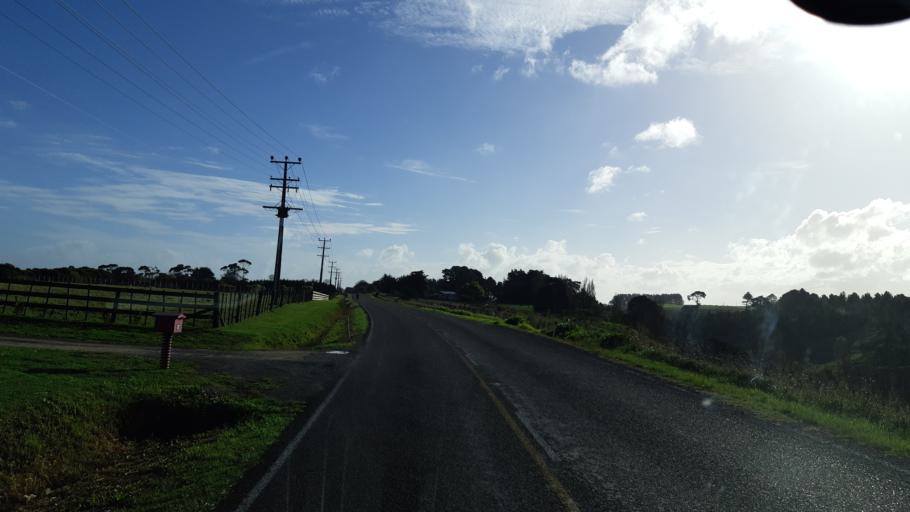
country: NZ
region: Manawatu-Wanganui
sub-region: Wanganui District
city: Wanganui
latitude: -39.9377
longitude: 175.1109
